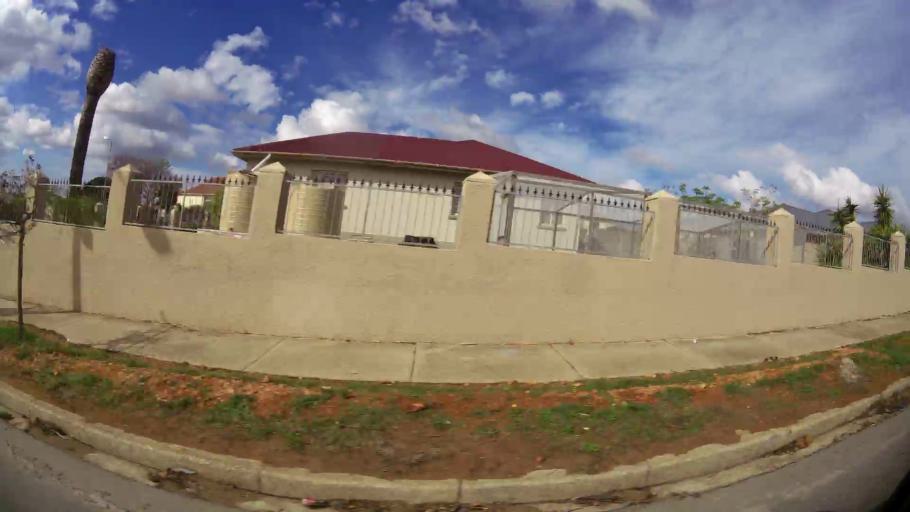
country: ZA
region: Eastern Cape
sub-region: Nelson Mandela Bay Metropolitan Municipality
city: Port Elizabeth
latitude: -33.9414
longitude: 25.5709
